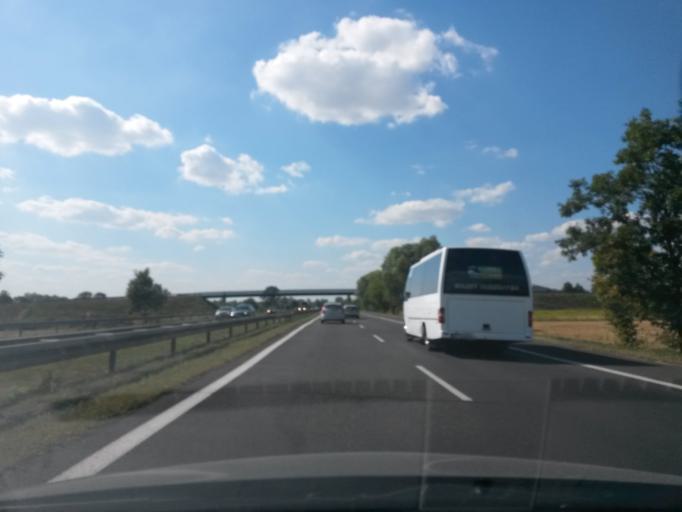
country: PL
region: Masovian Voivodeship
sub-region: Powiat nowodworski
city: Nowy Dwor Mazowiecki
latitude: 52.4162
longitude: 20.6819
